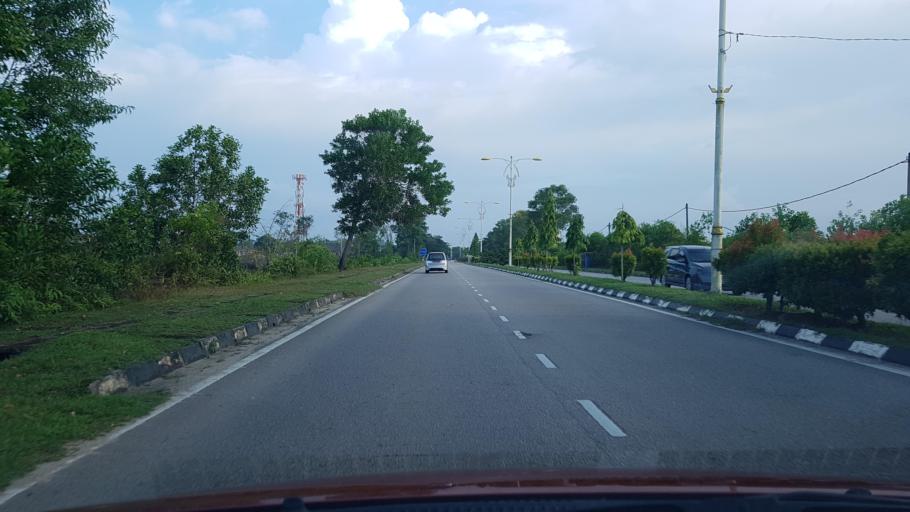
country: MY
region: Terengganu
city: Kuala Terengganu
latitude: 5.3539
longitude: 103.1034
